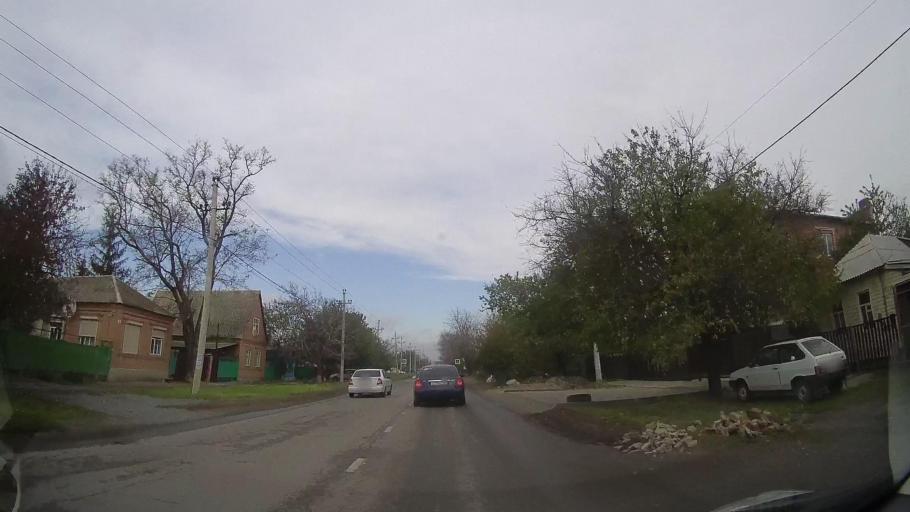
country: RU
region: Rostov
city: Bataysk
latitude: 47.1448
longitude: 39.7670
